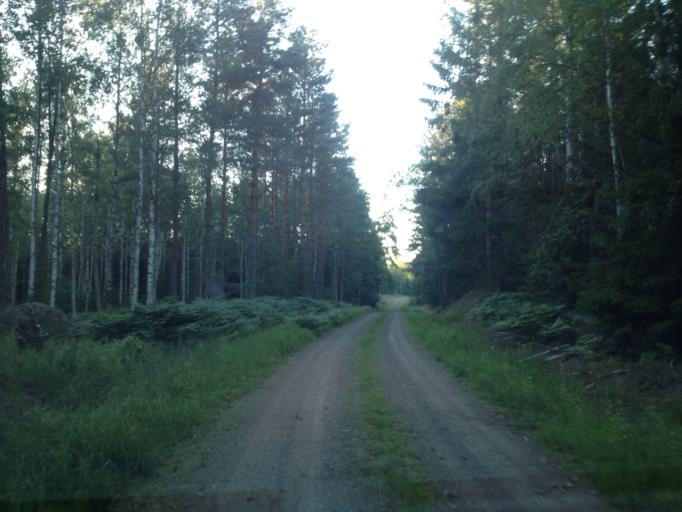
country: SE
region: Kalmar
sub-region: Vasterviks Kommun
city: Overum
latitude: 57.9934
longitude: 16.1700
